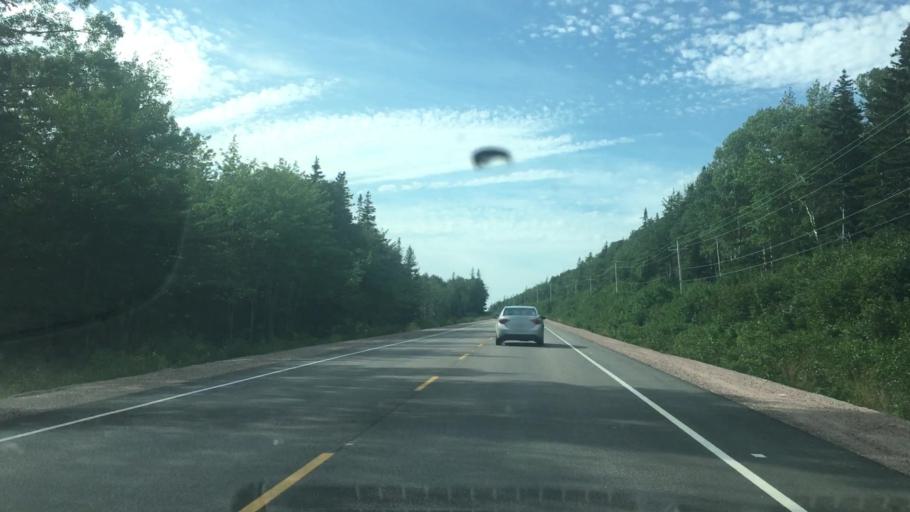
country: CA
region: Nova Scotia
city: Sydney Mines
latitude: 46.8162
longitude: -60.3439
